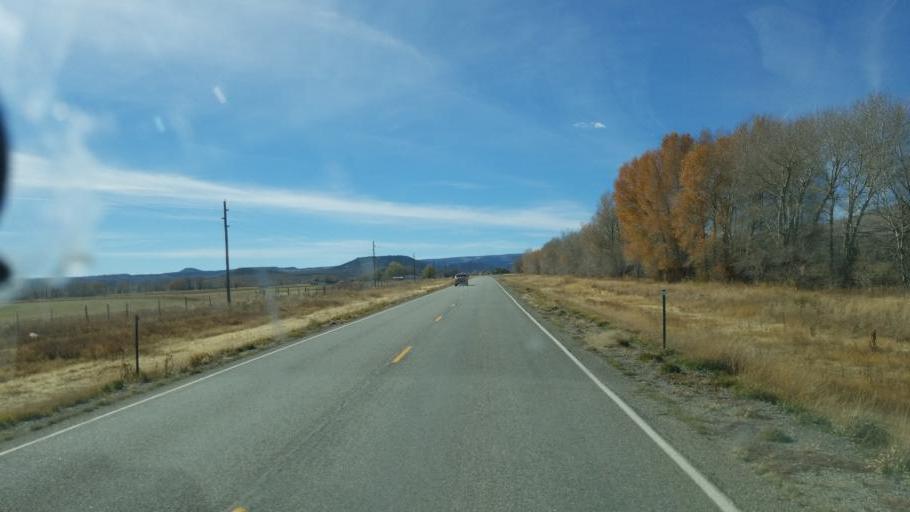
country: US
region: Colorado
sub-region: Conejos County
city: Conejos
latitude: 37.0621
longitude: -106.0811
